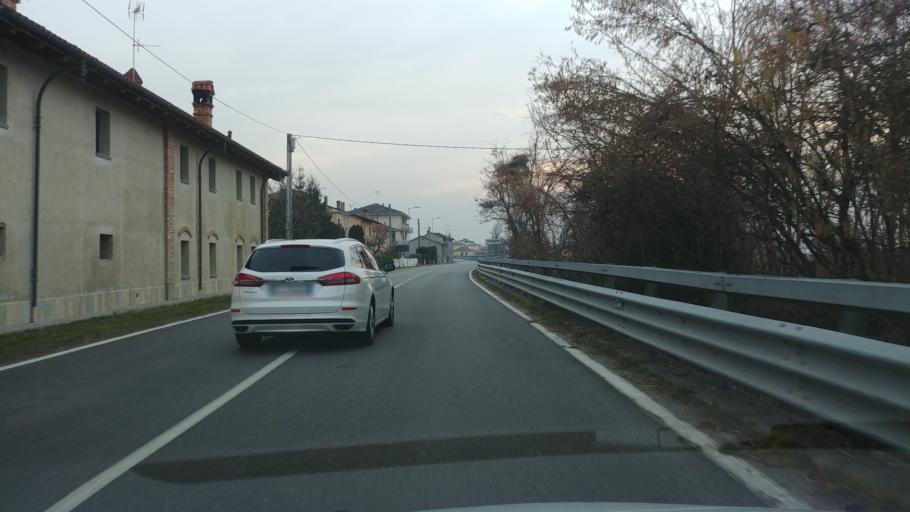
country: IT
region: Piedmont
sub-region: Provincia di Cuneo
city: Montanera
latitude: 44.4865
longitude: 7.6548
